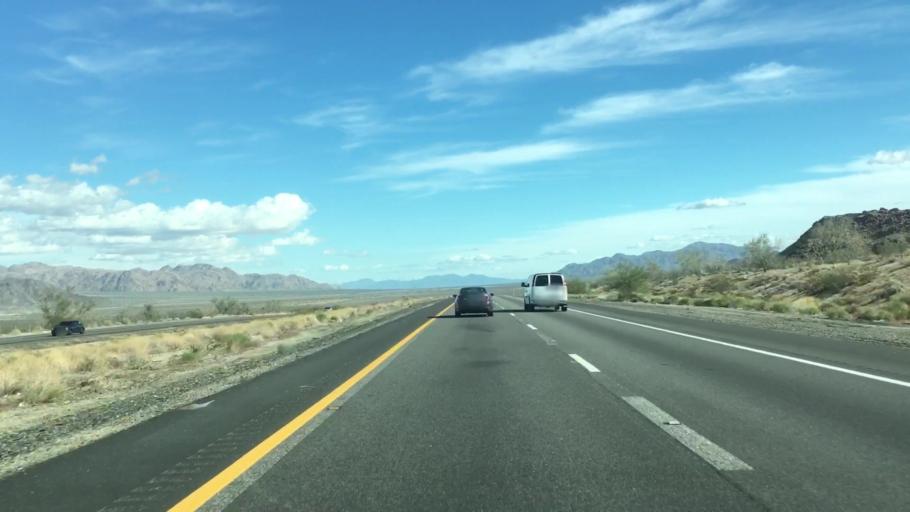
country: US
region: California
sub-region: Riverside County
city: Mecca
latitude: 33.6654
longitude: -115.6869
